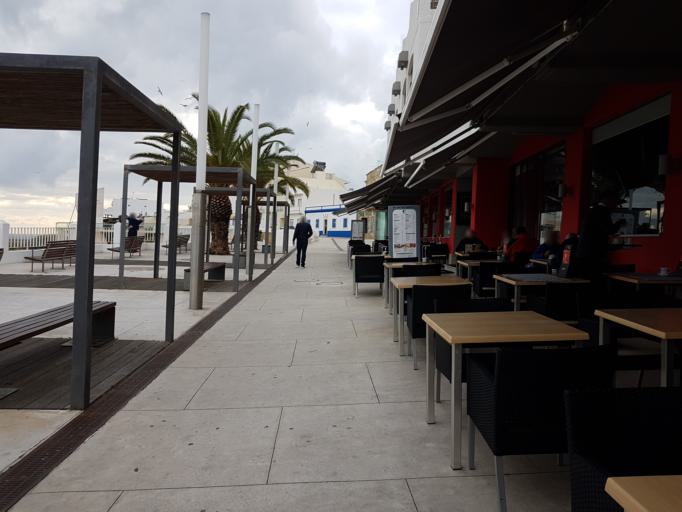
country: PT
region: Faro
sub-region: Albufeira
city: Albufeira
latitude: 37.0866
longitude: -8.2550
